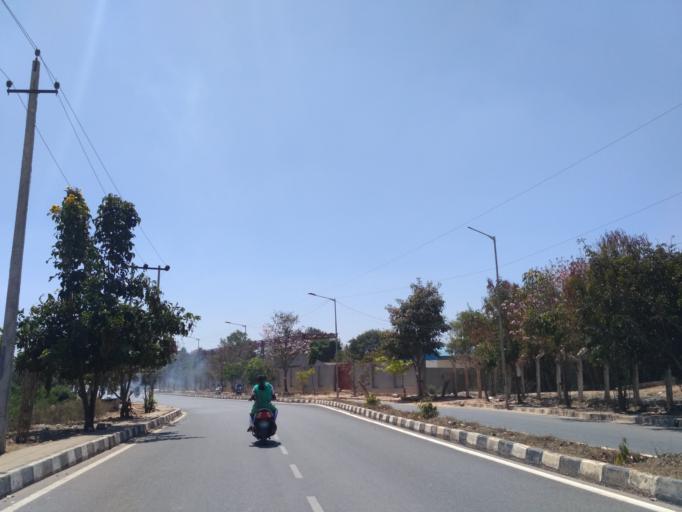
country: IN
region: Karnataka
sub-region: Bangalore Urban
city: Yelahanka
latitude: 13.0913
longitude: 77.5903
